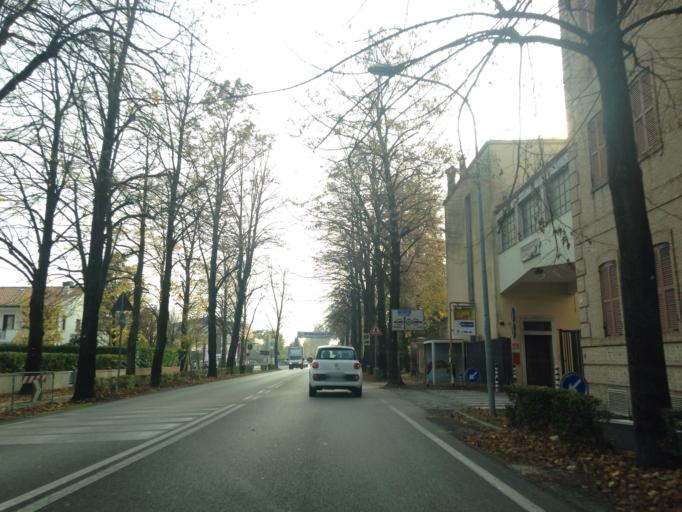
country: IT
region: Veneto
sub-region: Provincia di Treviso
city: Oderzo
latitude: 45.7722
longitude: 12.4885
